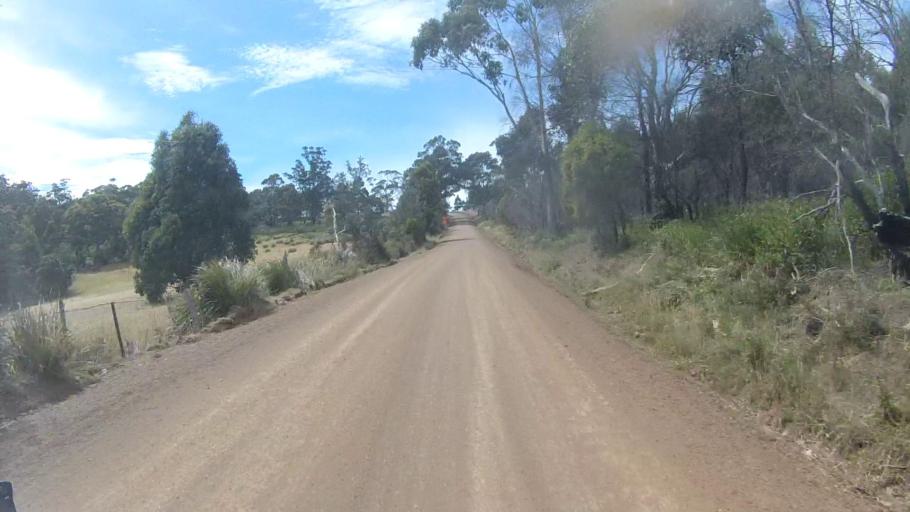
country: AU
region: Tasmania
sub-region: Sorell
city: Sorell
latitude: -42.7798
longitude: 147.8400
